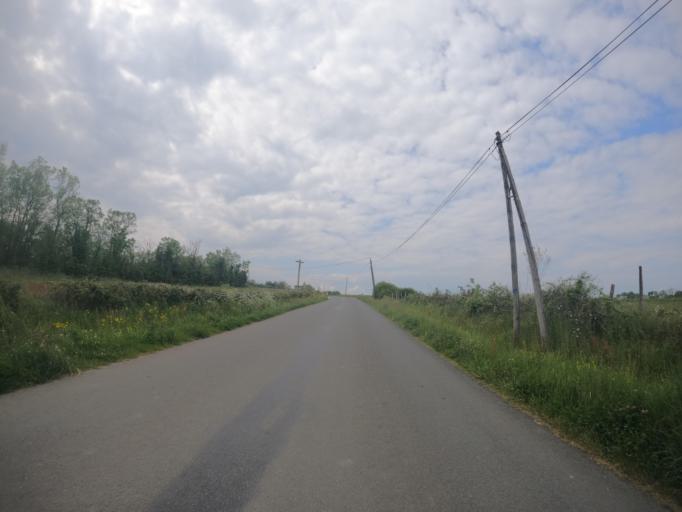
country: FR
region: Poitou-Charentes
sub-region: Departement des Deux-Sevres
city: Saint-Varent
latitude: 46.8605
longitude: -0.2639
